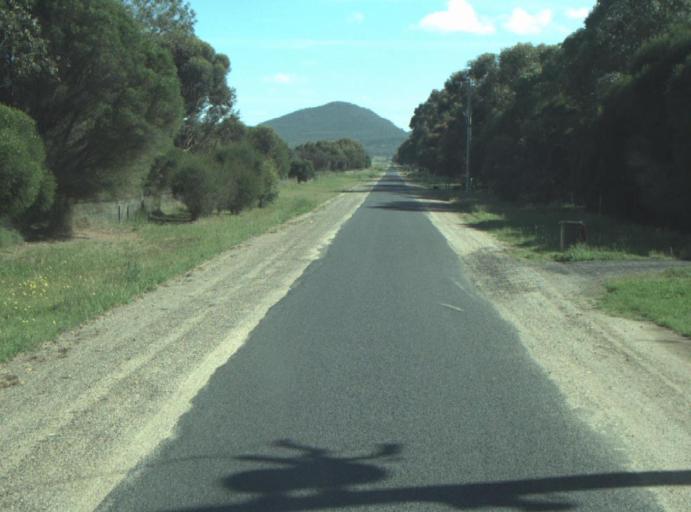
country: AU
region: Victoria
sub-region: Greater Geelong
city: Lara
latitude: -37.9998
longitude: 144.4193
